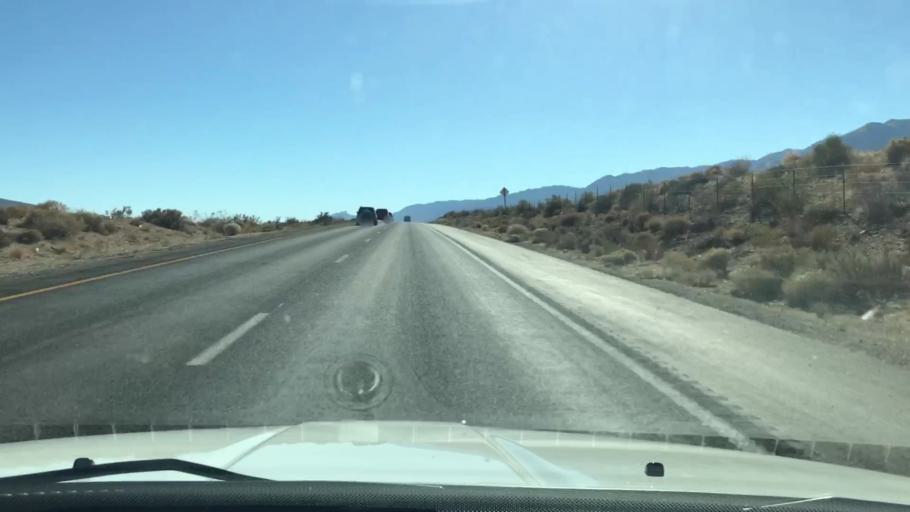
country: US
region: California
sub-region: Inyo County
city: Lone Pine
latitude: 36.2015
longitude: -117.9794
